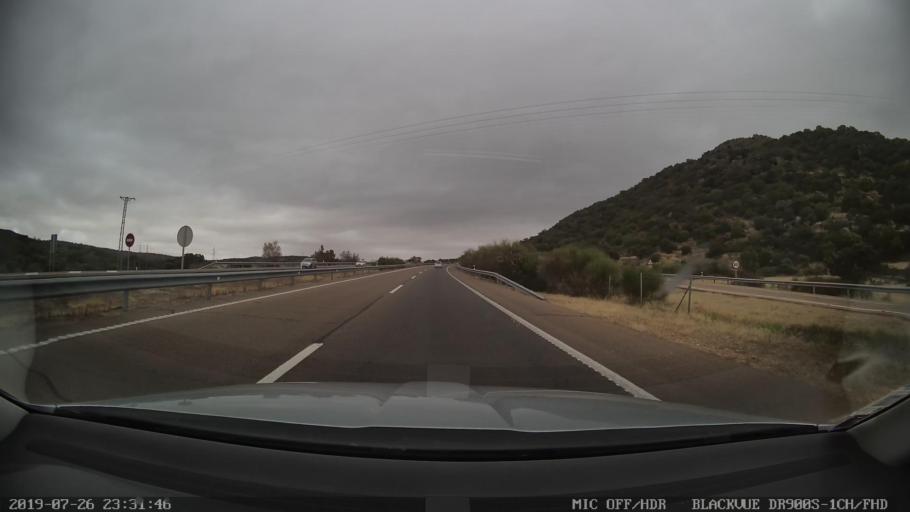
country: ES
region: Extremadura
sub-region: Provincia de Caceres
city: Puerto de Santa Cruz
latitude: 39.3055
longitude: -5.8573
